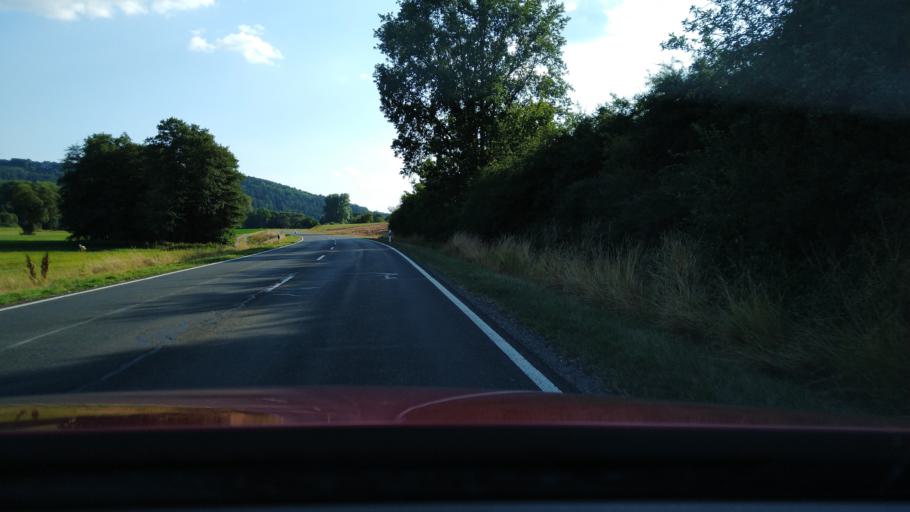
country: DE
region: Bavaria
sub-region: Upper Franconia
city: Plankenfels
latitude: 49.8992
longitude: 11.3652
